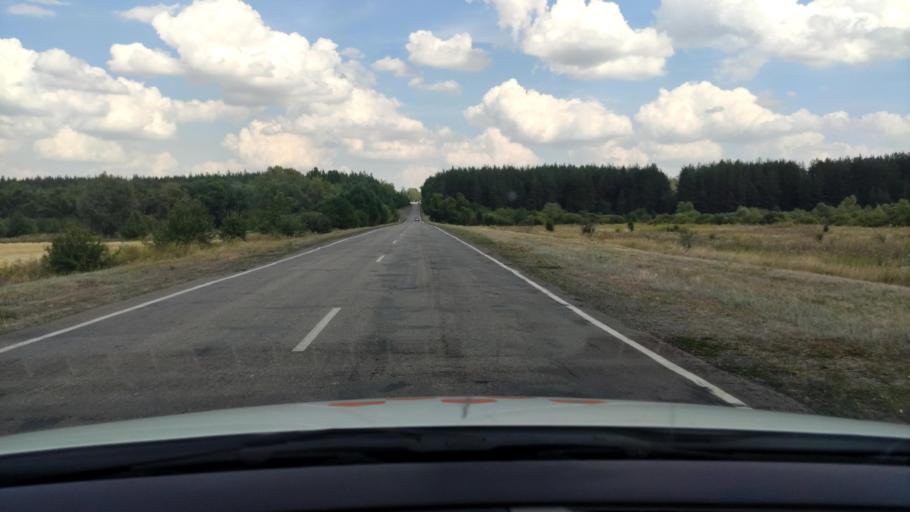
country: RU
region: Voronezj
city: Sadovoye
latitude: 51.7779
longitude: 40.5286
